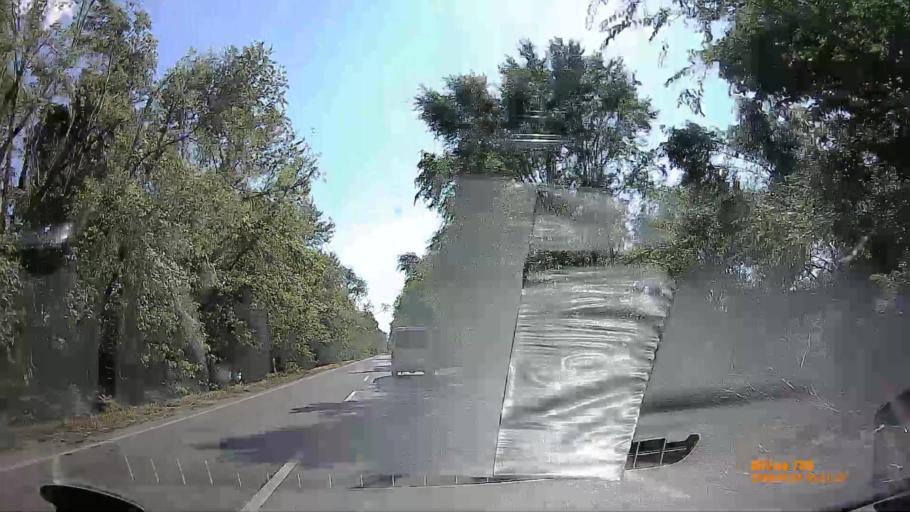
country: HU
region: Szabolcs-Szatmar-Bereg
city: Nyirmada
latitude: 48.0385
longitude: 22.1799
